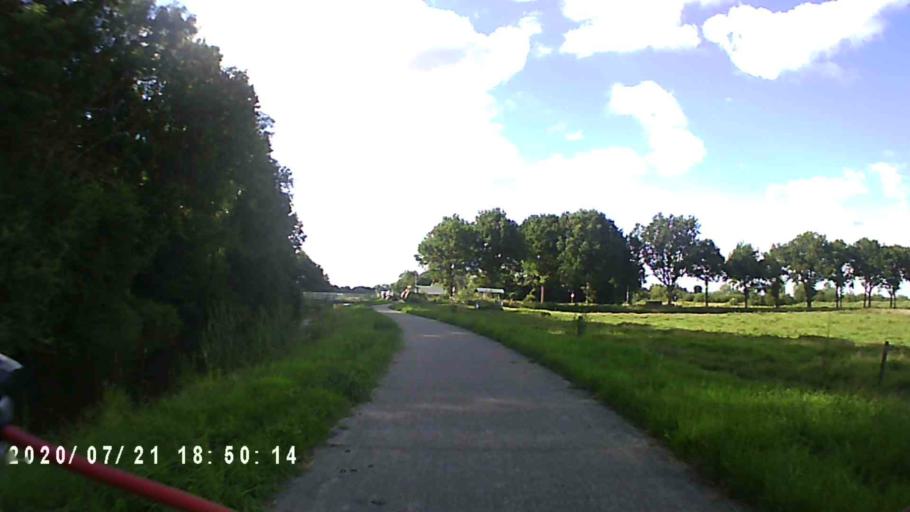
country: NL
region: Groningen
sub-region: Gemeente Hoogezand-Sappemeer
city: Hoogezand
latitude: 53.2186
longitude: 6.7425
